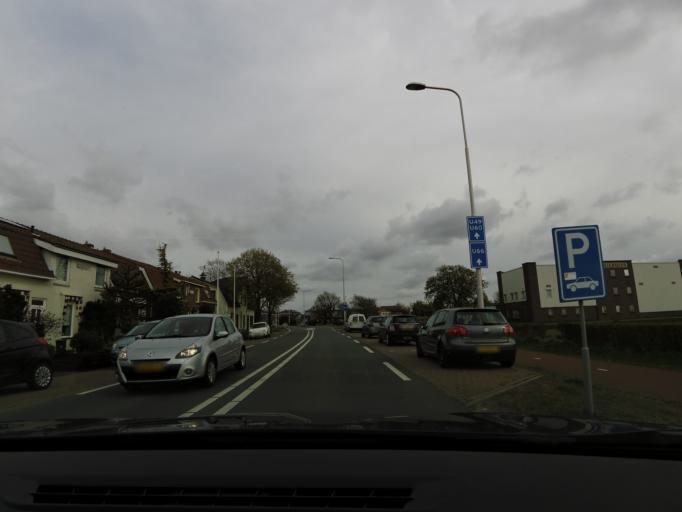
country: NL
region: South Holland
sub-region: Gemeente Teylingen
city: Sassenheim
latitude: 52.2337
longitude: 4.5182
